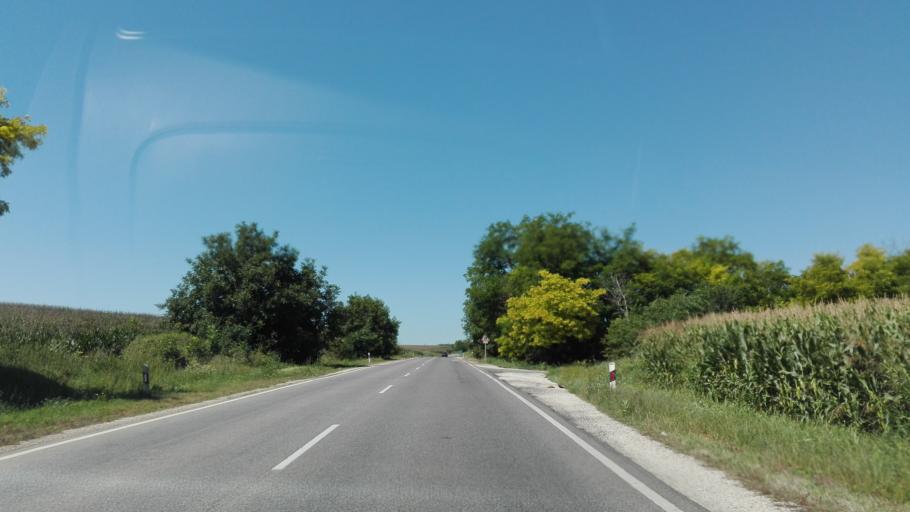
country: HU
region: Fejer
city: Mezoszilas
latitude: 46.8315
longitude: 18.4654
